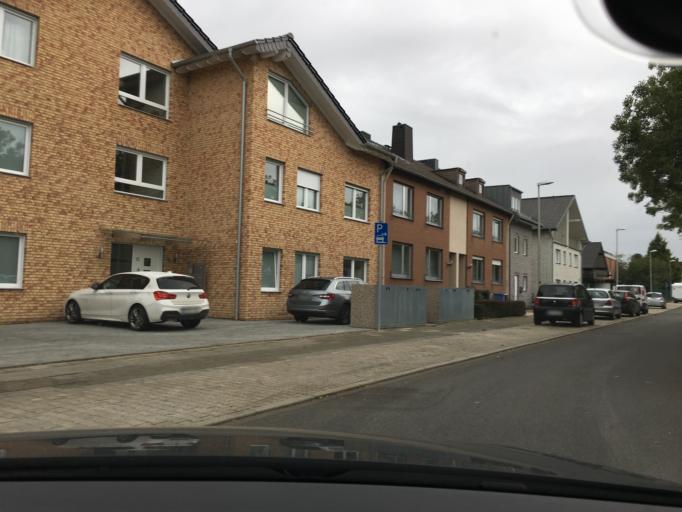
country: DE
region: North Rhine-Westphalia
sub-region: Regierungsbezirk Koln
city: Dueren
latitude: 50.7890
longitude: 6.4703
